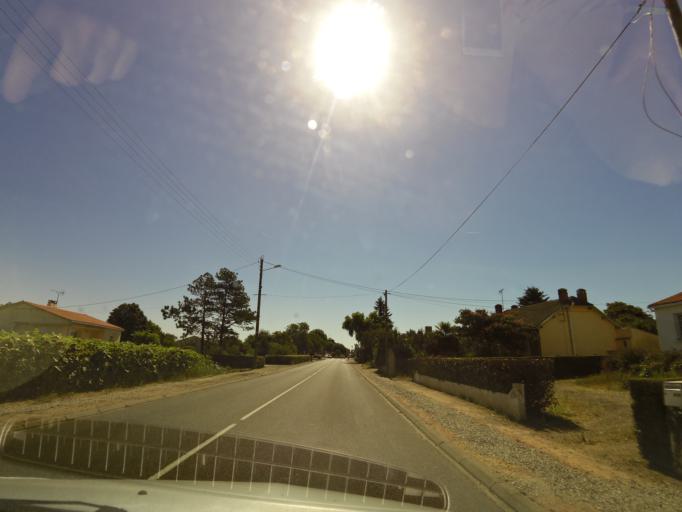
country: FR
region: Pays de la Loire
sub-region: Departement de la Vendee
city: Jard-sur-Mer
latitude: 46.4170
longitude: -1.5500
